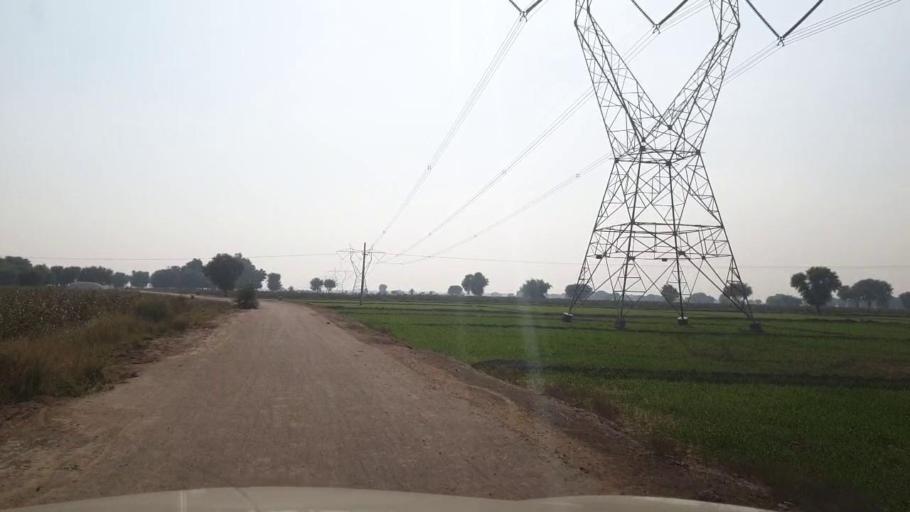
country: PK
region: Sindh
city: Bhan
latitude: 26.5432
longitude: 67.7489
